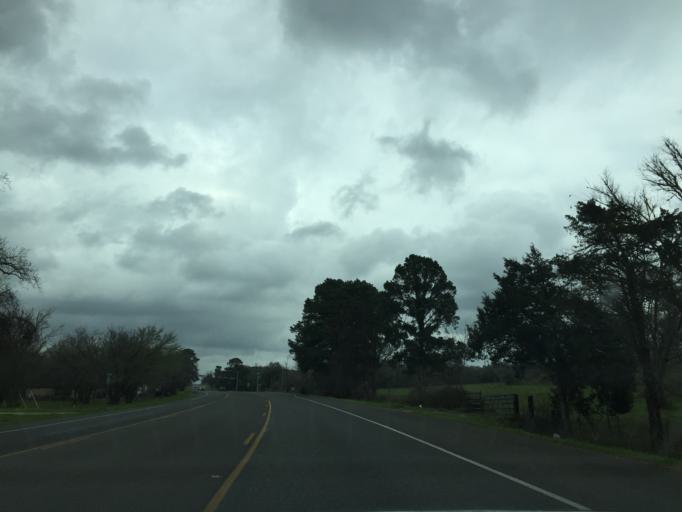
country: US
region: Texas
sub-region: Bastrop County
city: Bastrop
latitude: 30.1187
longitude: -97.3083
